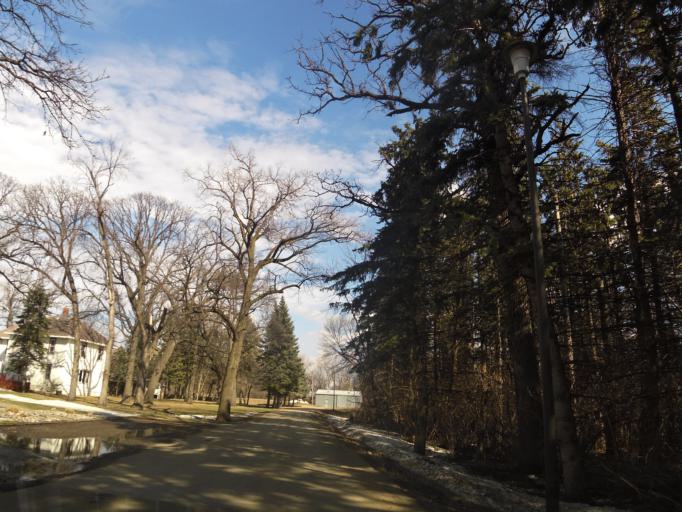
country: US
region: North Dakota
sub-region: Walsh County
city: Grafton
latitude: 48.4219
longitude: -97.3953
